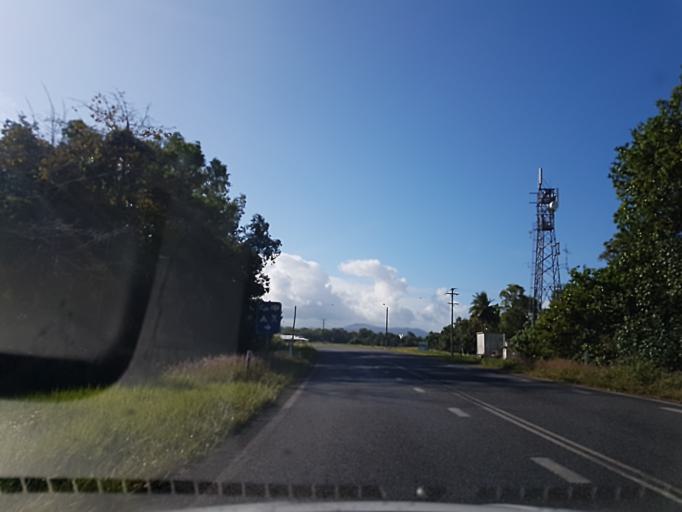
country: AU
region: Queensland
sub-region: Cairns
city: Port Douglas
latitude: -16.3477
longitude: 145.4094
